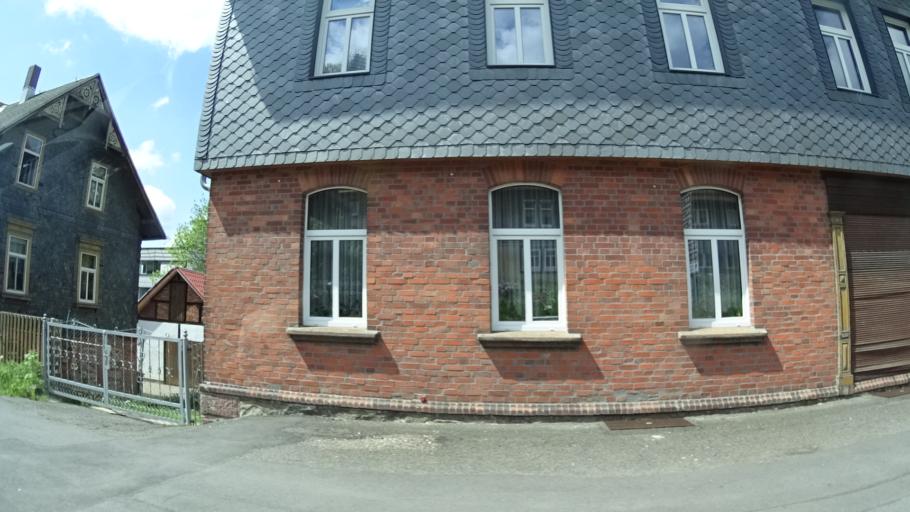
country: DE
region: Thuringia
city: Suhl
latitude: 50.6167
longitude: 10.6991
